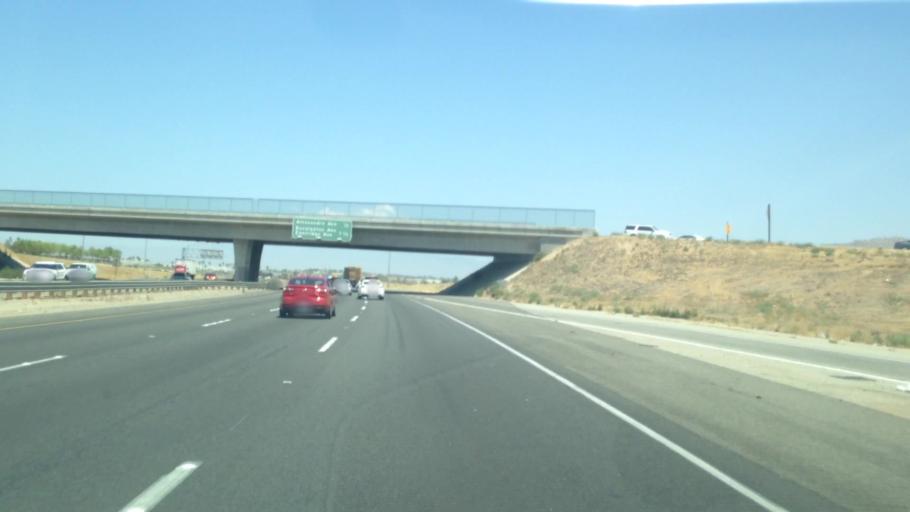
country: US
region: California
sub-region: Riverside County
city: March Air Force Base
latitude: 33.9085
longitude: -117.2796
